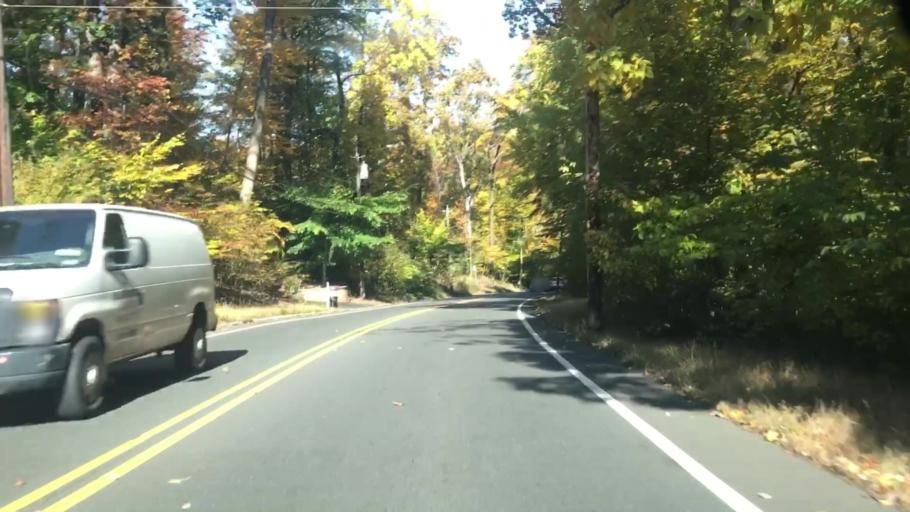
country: US
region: New Jersey
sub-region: Mercer County
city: Princeton
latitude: 40.3774
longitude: -74.6634
